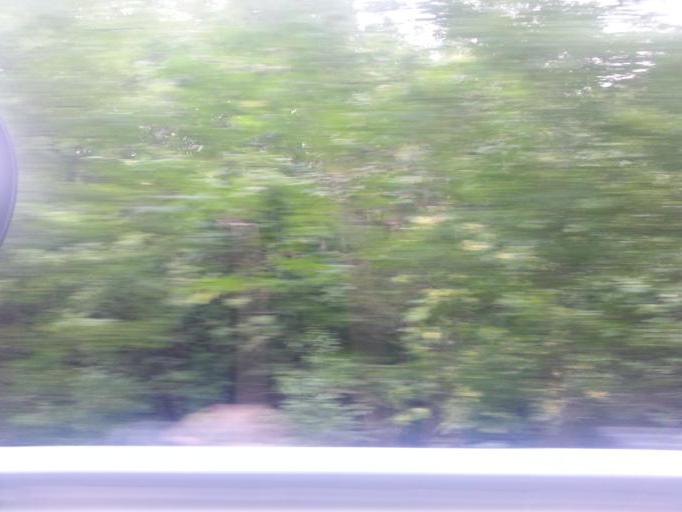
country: US
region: Tennessee
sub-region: Morgan County
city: Coalfield
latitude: 36.1102
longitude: -84.4421
